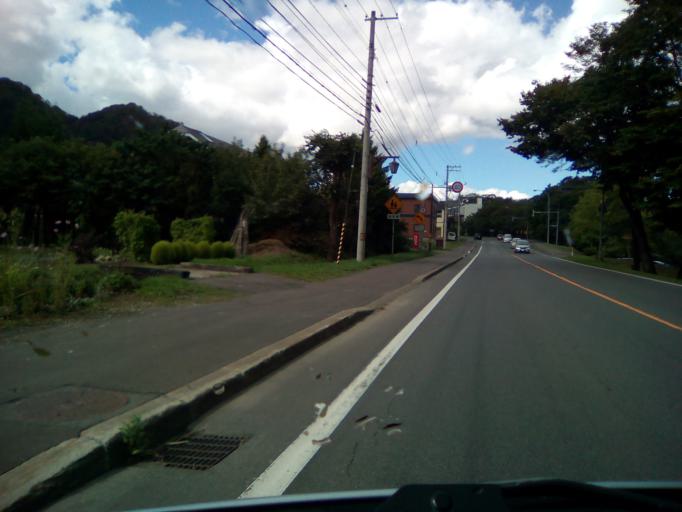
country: JP
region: Hokkaido
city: Date
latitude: 42.5683
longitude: 140.8053
